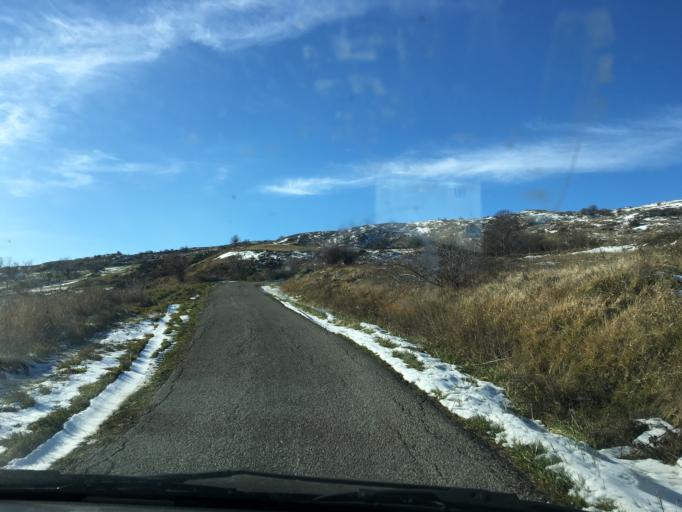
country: IT
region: Abruzzo
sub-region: Provincia di Chieti
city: Rosello
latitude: 41.8554
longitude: 14.3562
